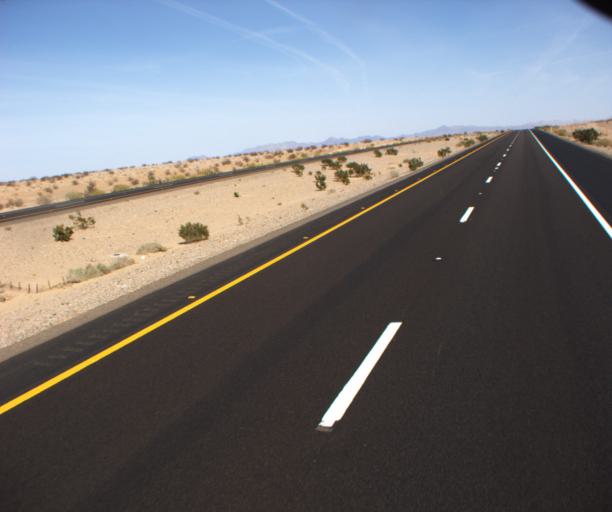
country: US
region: Arizona
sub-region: Yuma County
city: Somerton
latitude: 32.4951
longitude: -114.6141
